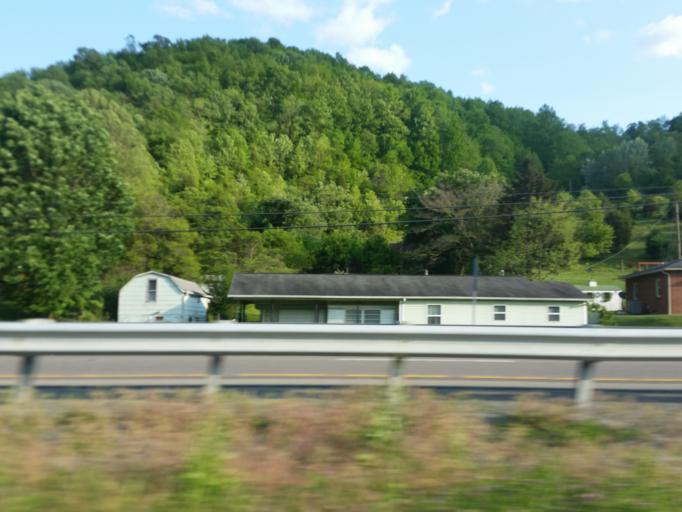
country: US
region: Virginia
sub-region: Russell County
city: Lebanon
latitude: 36.9106
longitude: -82.0275
